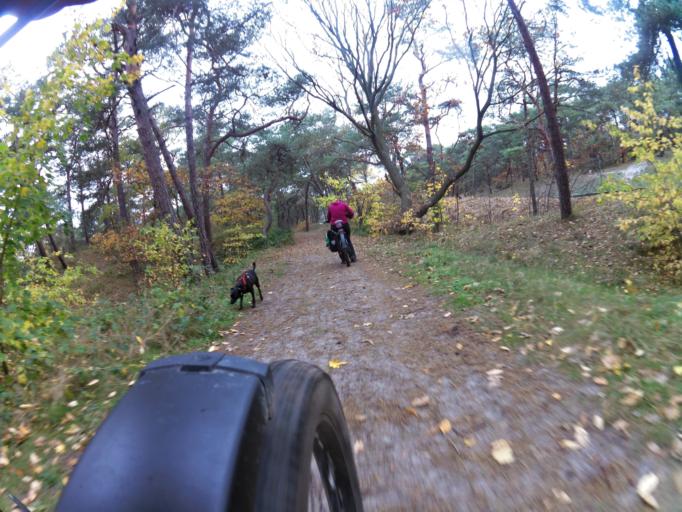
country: PL
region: Pomeranian Voivodeship
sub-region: Powiat pucki
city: Jastarnia
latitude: 54.6966
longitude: 18.6895
